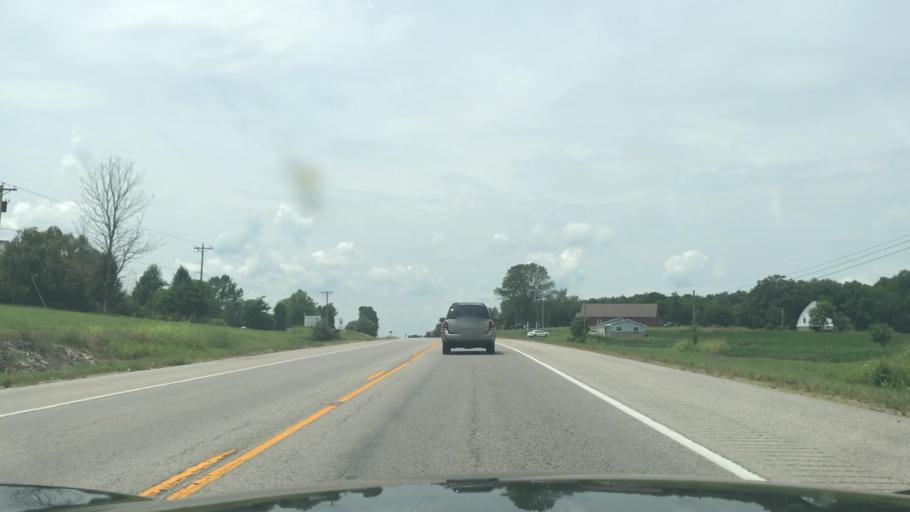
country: US
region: Kentucky
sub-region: Green County
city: Greensburg
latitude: 37.2923
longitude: -85.4721
